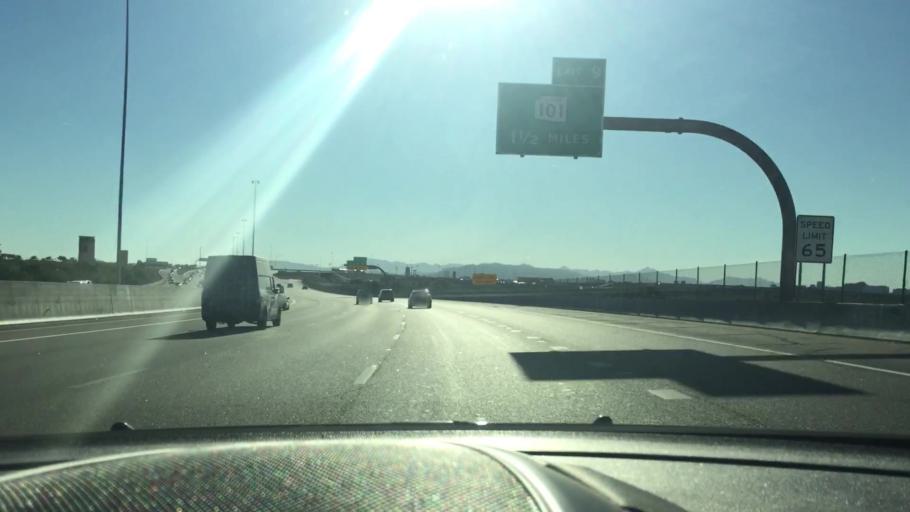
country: US
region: Arizona
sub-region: Maricopa County
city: Mesa
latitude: 33.4436
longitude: -111.8653
